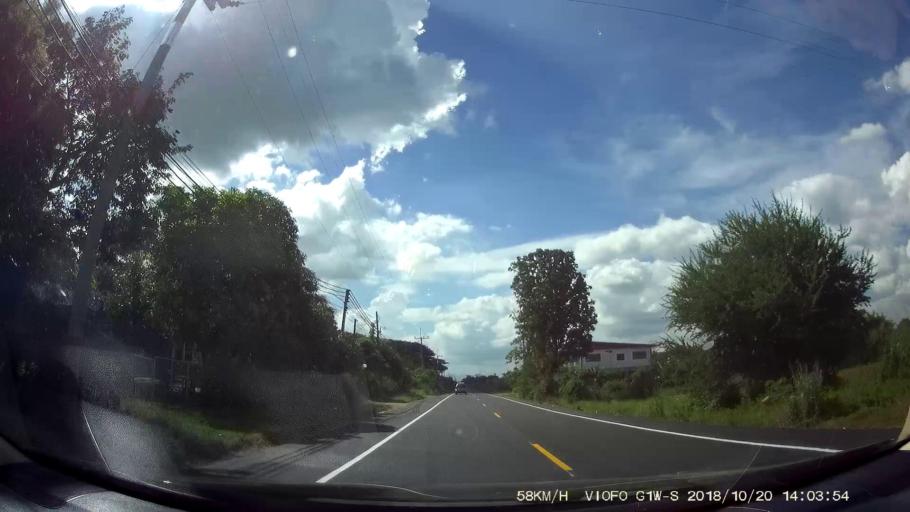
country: TH
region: Khon Kaen
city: Chum Phae
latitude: 16.4887
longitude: 102.1215
